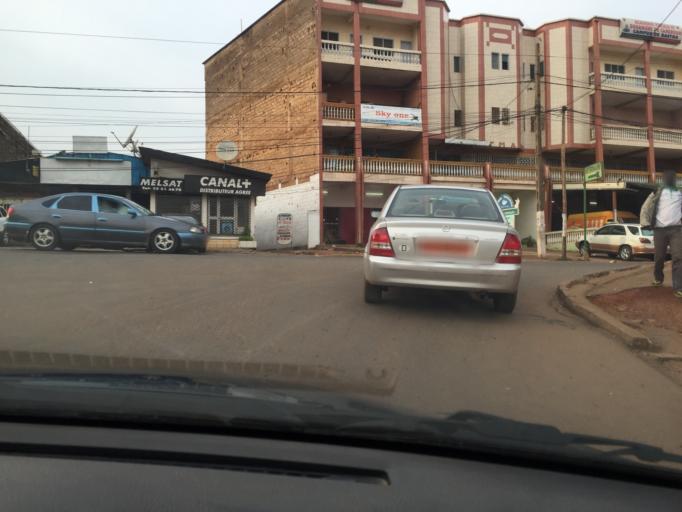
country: CM
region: Centre
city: Yaounde
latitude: 3.8853
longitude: 11.5179
